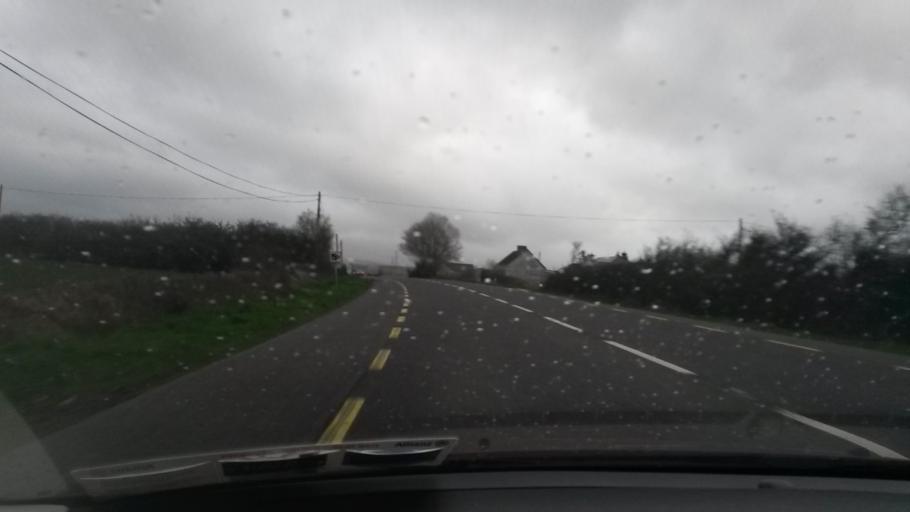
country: IE
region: Munster
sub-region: County Limerick
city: Abbeyfeale
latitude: 52.3625
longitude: -9.3250
